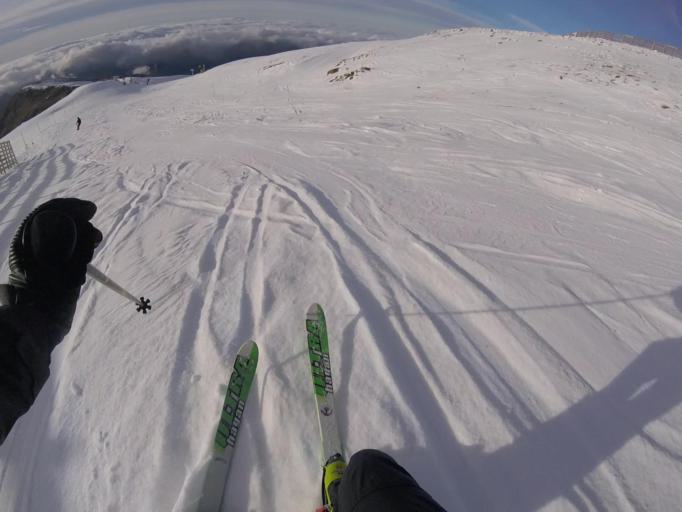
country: ES
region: Andalusia
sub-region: Provincia de Granada
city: Guejar-Sierra
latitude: 37.0708
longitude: -3.3997
